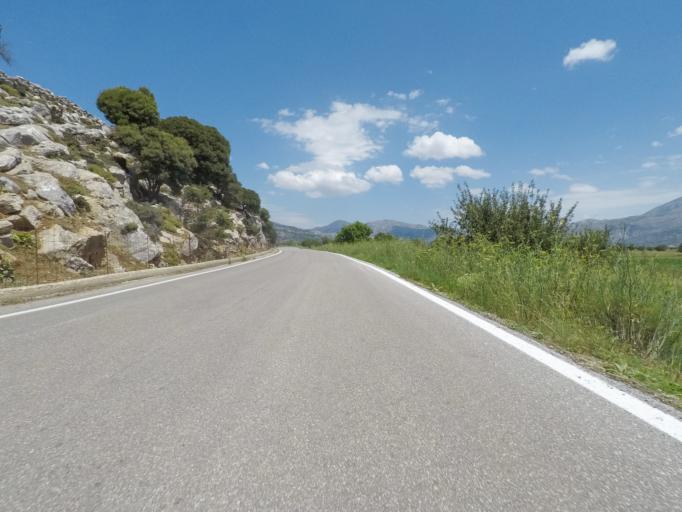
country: GR
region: Crete
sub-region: Nomos Irakleiou
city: Mokhos
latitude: 35.1961
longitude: 25.4568
